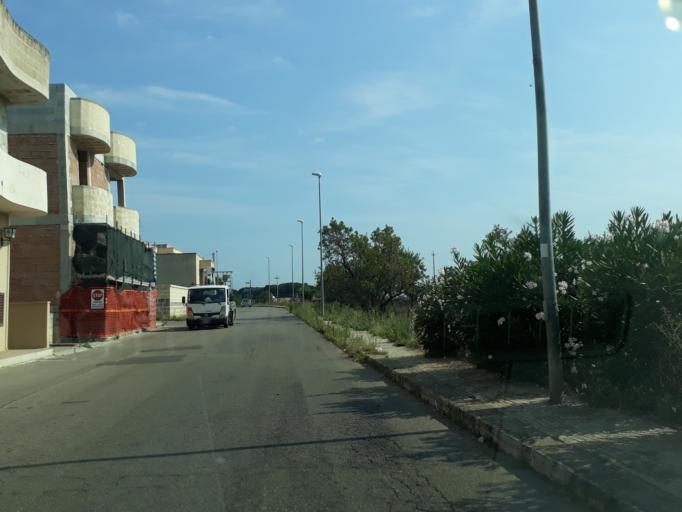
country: IT
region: Apulia
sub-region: Provincia di Brindisi
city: Carovigno
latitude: 40.6997
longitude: 17.6678
